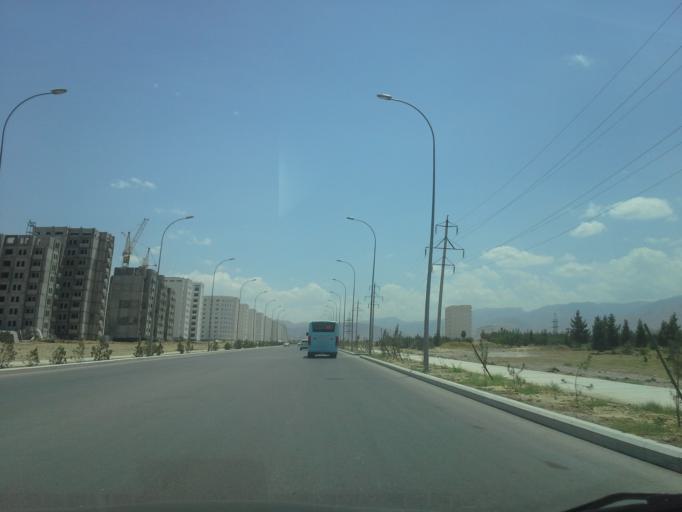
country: TM
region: Ahal
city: Ashgabat
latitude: 37.8994
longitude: 58.4058
